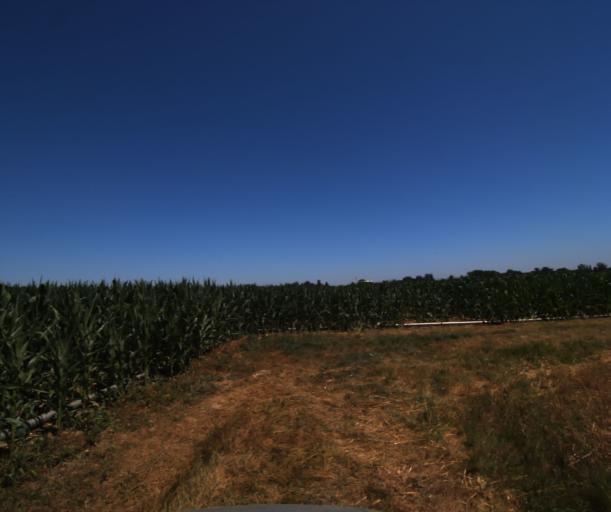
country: FR
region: Midi-Pyrenees
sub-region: Departement de la Haute-Garonne
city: Seysses
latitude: 43.4679
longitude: 1.2915
